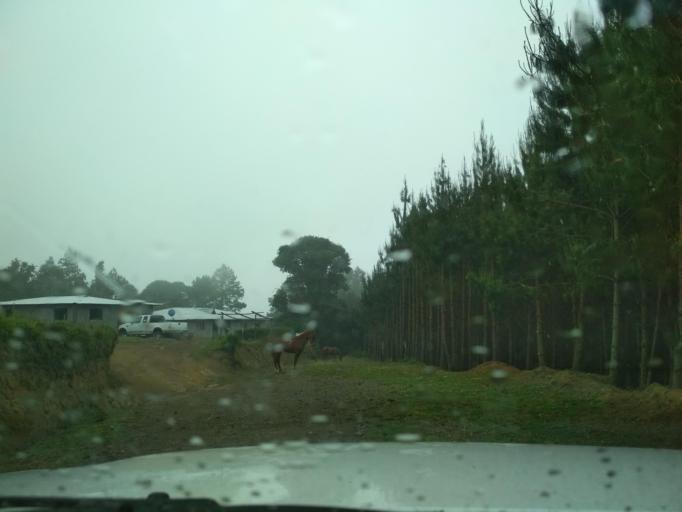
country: MX
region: Veracruz
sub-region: Mariano Escobedo
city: Loma Grande
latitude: 18.9256
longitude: -97.2184
